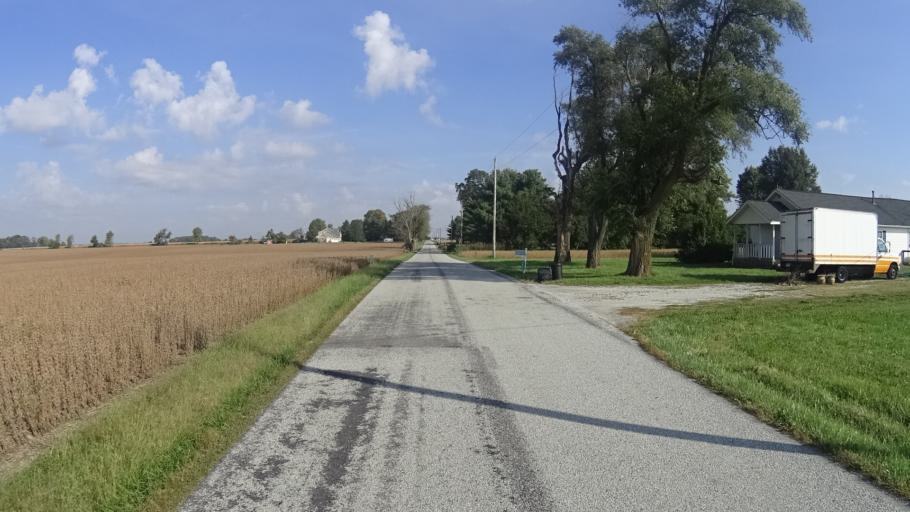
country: US
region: Indiana
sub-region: Madison County
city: Lapel
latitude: 40.0359
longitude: -85.8625
